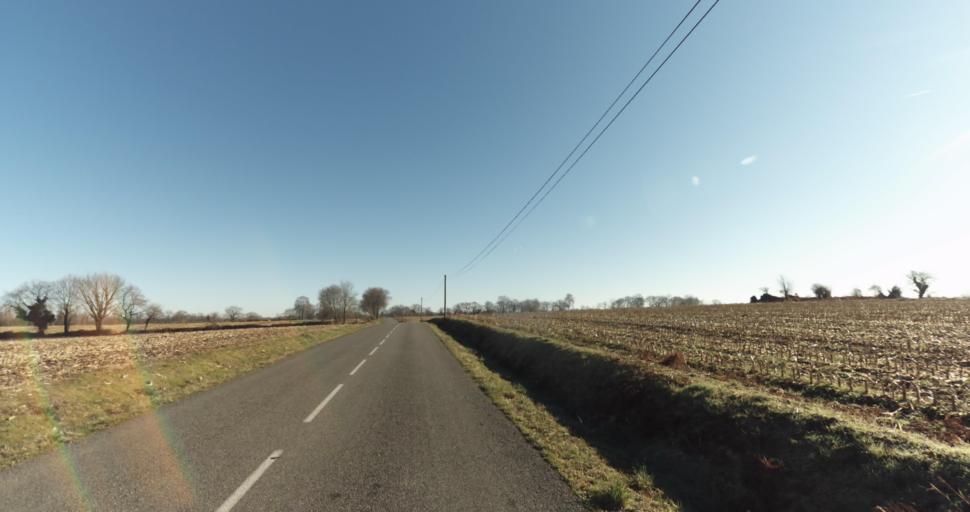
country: FR
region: Aquitaine
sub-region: Departement des Pyrenees-Atlantiques
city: Morlaas
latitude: 43.3404
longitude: -0.2300
